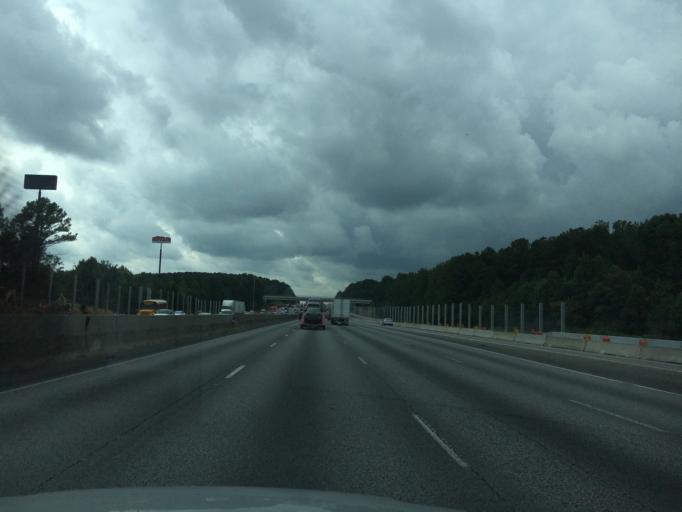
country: US
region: Georgia
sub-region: Gwinnett County
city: Suwanee
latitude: 34.0289
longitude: -84.0499
